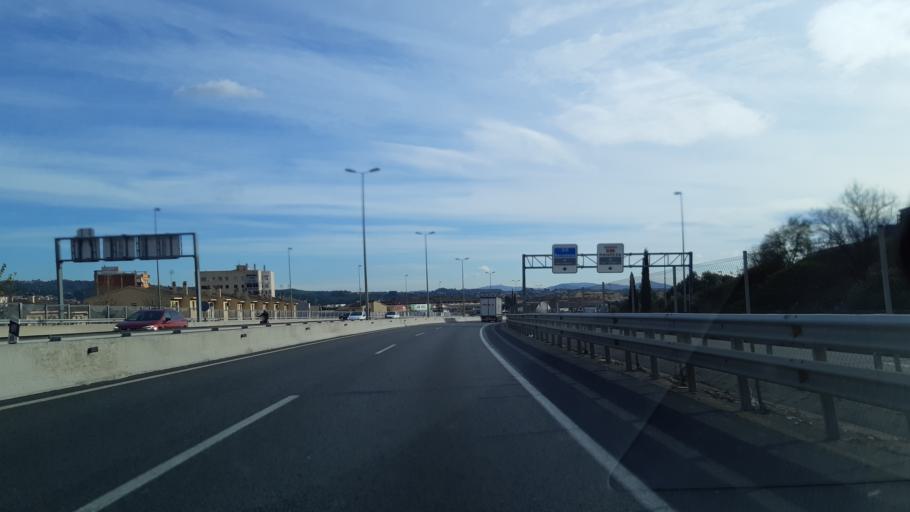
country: ES
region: Catalonia
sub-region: Provincia de Barcelona
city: Abrera
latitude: 41.5214
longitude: 1.8925
